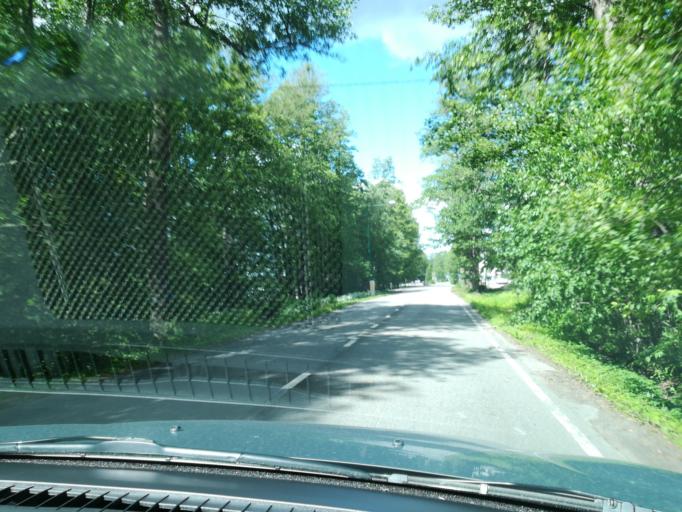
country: FI
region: Southern Savonia
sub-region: Mikkeli
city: Hirvensalmi
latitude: 61.6394
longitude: 26.7772
